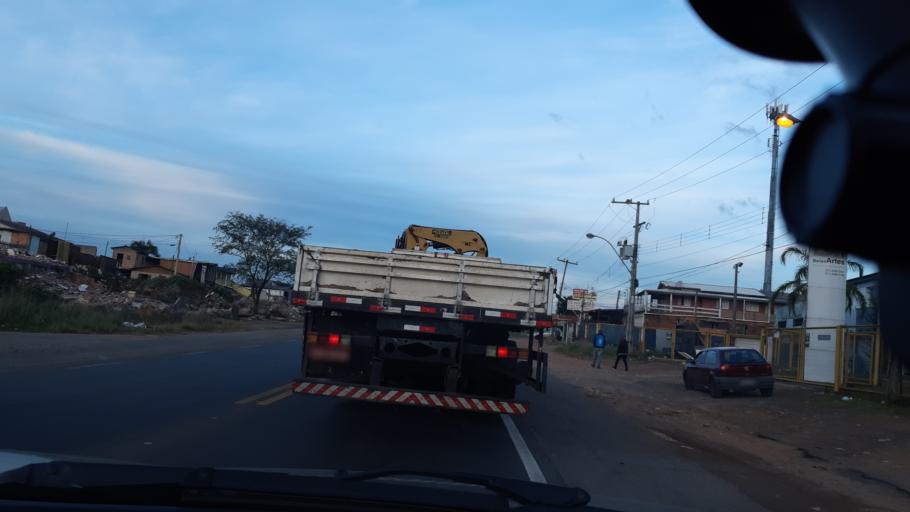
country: BR
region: Rio Grande do Sul
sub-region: Sapucaia Do Sul
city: Sapucaia
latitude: -29.8368
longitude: -51.1566
